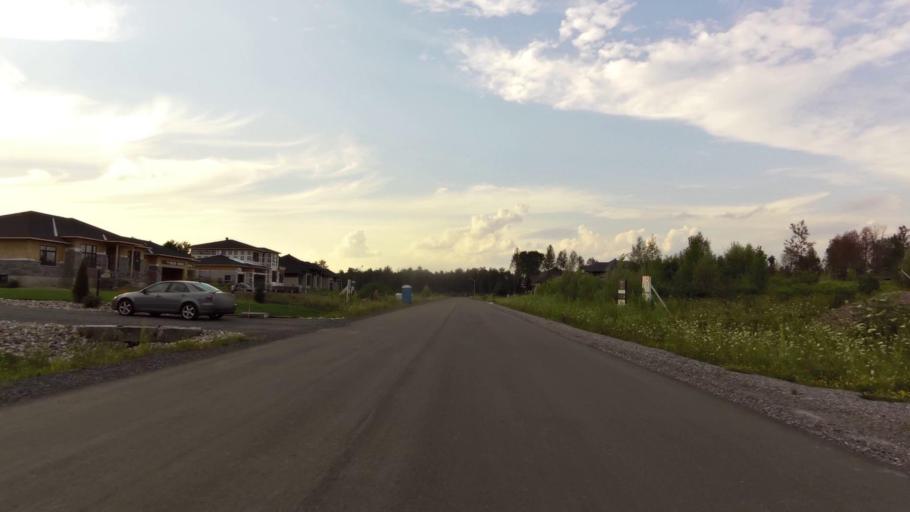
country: CA
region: Ontario
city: Ottawa
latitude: 45.2655
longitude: -75.5838
